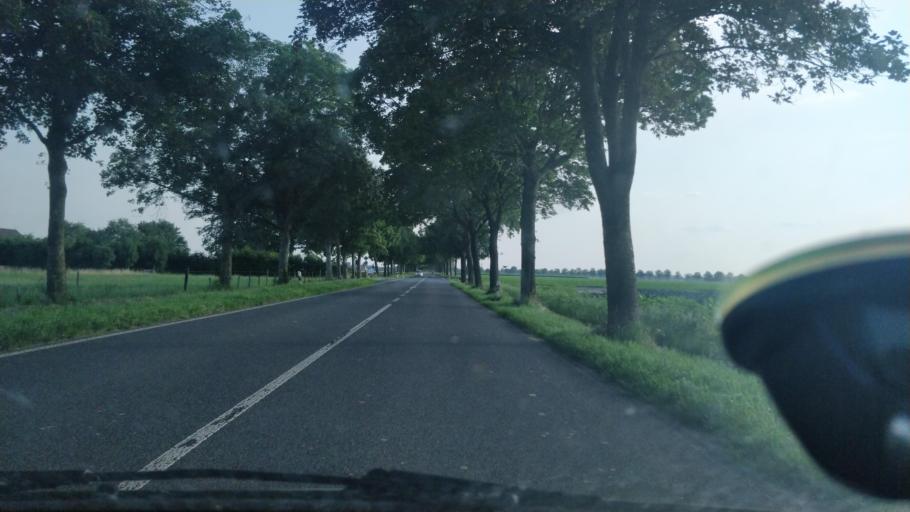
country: DE
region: North Rhine-Westphalia
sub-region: Regierungsbezirk Dusseldorf
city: Rheurdt
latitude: 51.4546
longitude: 6.4302
